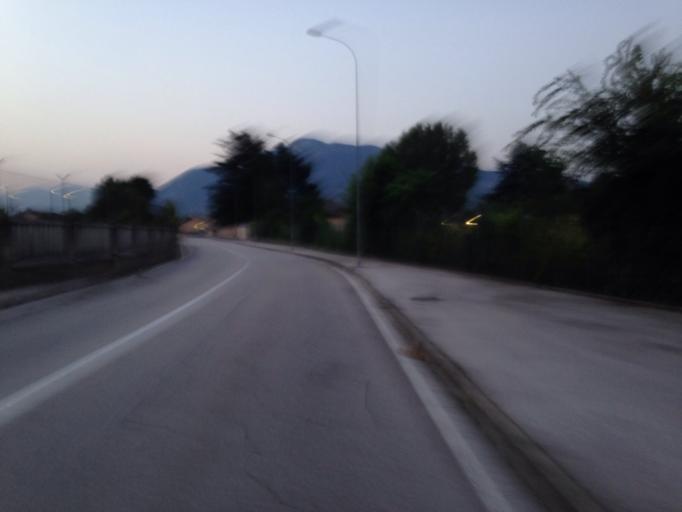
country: IT
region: Trentino-Alto Adige
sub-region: Provincia di Trento
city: Ravina
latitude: 46.0483
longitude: 11.1165
